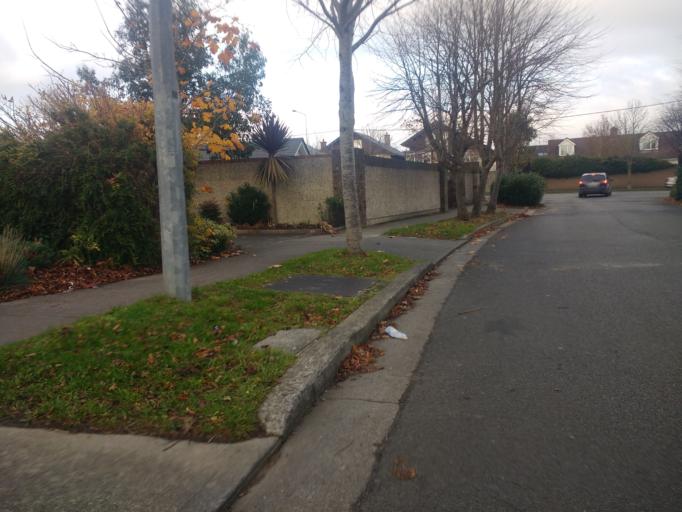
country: IE
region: Leinster
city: Kinsealy-Drinan
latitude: 53.4490
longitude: -6.1836
